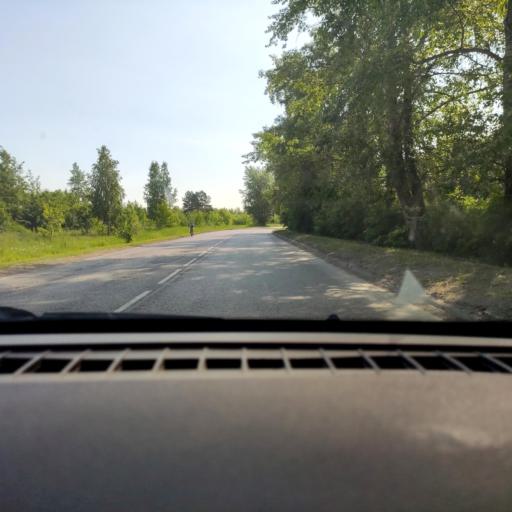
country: RU
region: Perm
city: Overyata
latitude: 57.9951
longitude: 55.9013
